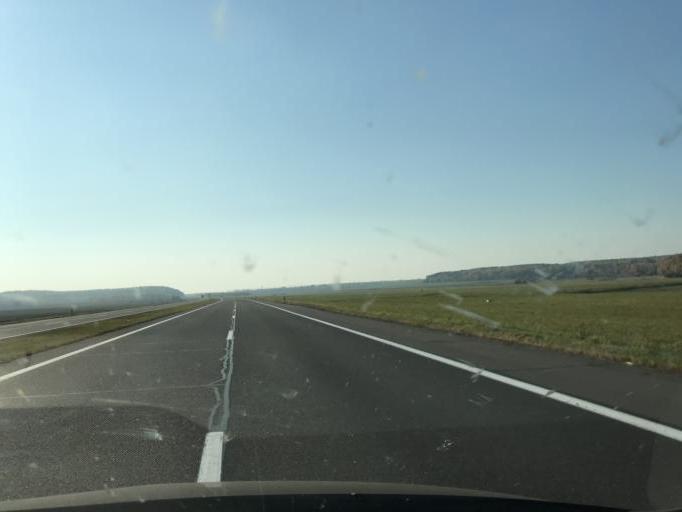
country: BY
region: Minsk
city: Snow
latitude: 53.2556
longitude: 26.2364
